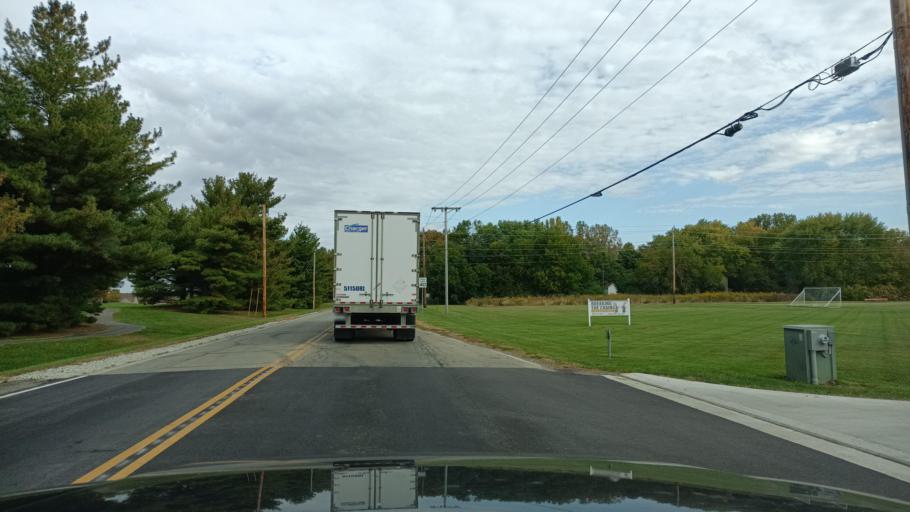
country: US
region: Indiana
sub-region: Delaware County
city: Yorktown
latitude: 40.1883
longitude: -85.4618
